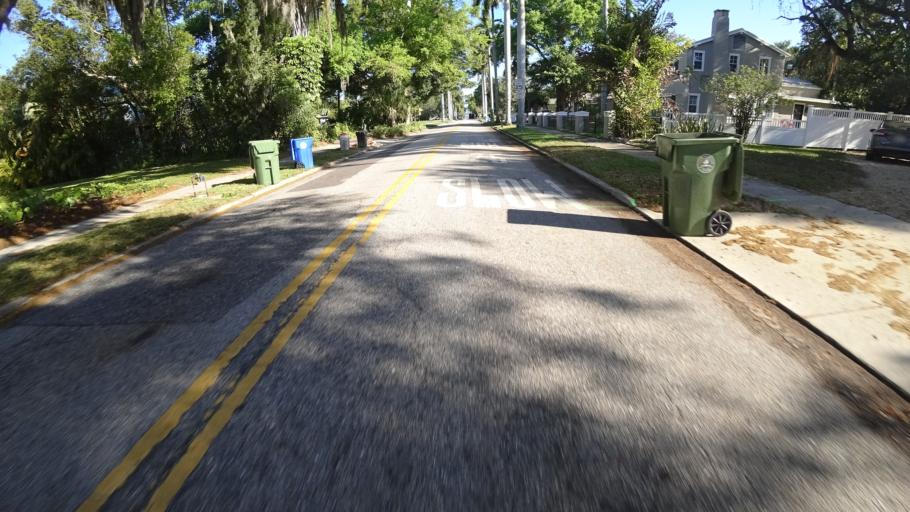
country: US
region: Florida
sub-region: Manatee County
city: Bradenton
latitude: 27.4964
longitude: -82.5874
